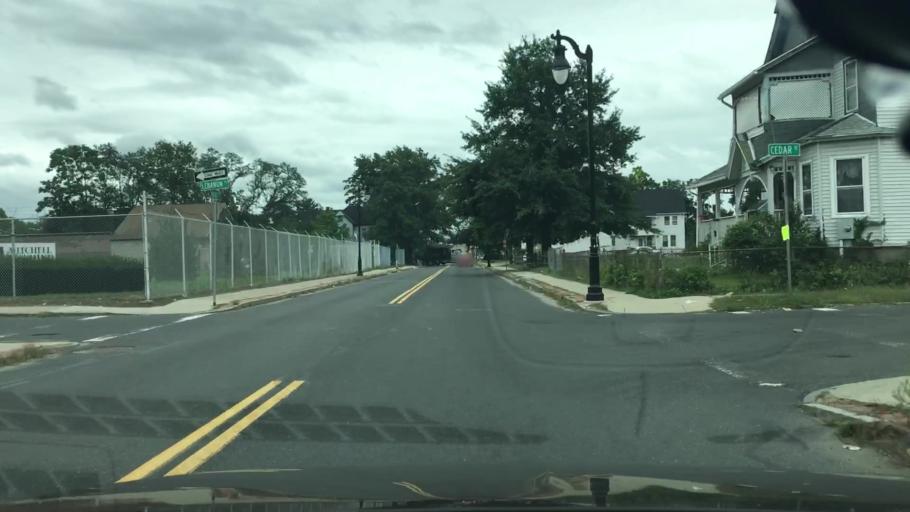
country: US
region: Massachusetts
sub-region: Hampden County
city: Springfield
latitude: 42.1029
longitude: -72.5697
